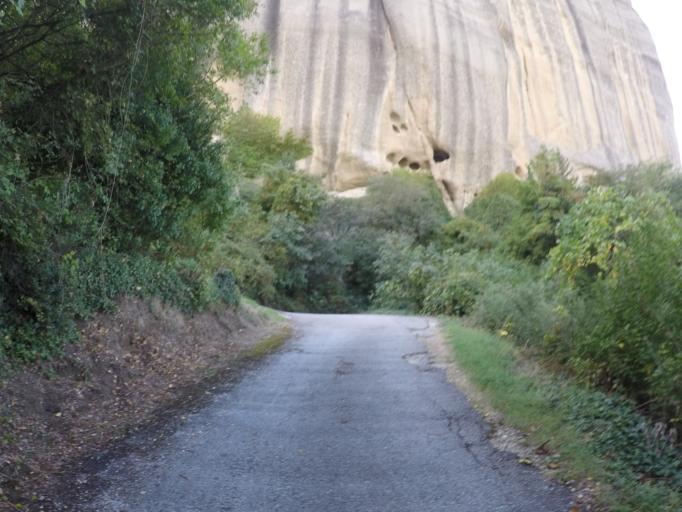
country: GR
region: Thessaly
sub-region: Trikala
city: Kastraki
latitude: 39.7142
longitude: 21.6234
